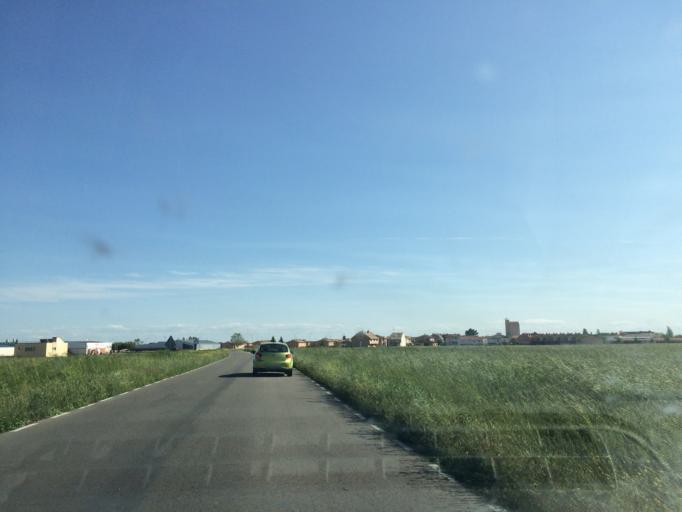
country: ES
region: Madrid
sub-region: Provincia de Madrid
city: Ribatejada
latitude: 40.7104
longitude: -3.4243
